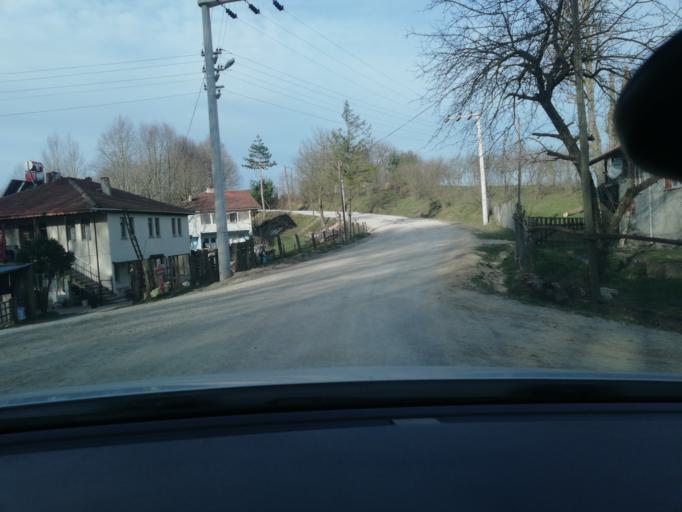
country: TR
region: Duzce
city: Konuralp
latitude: 40.9841
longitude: 31.2309
